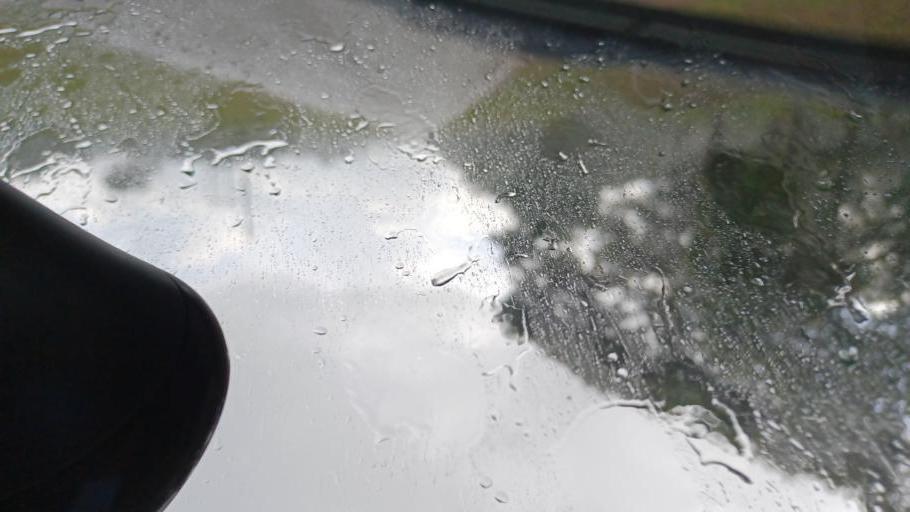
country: ZM
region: North-Western
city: Kasempa
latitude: -13.0969
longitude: 25.9083
